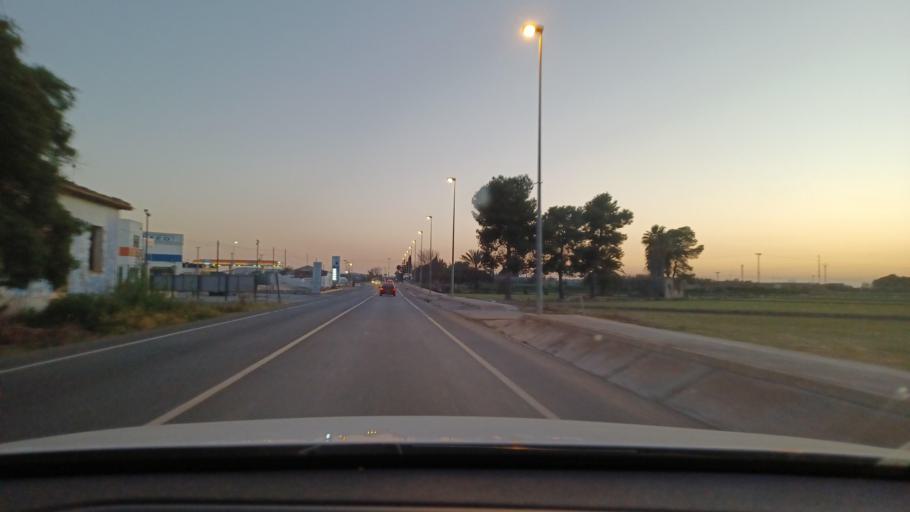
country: ES
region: Valencia
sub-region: Provincia de Alicante
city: Dolores
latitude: 38.1323
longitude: -0.7750
